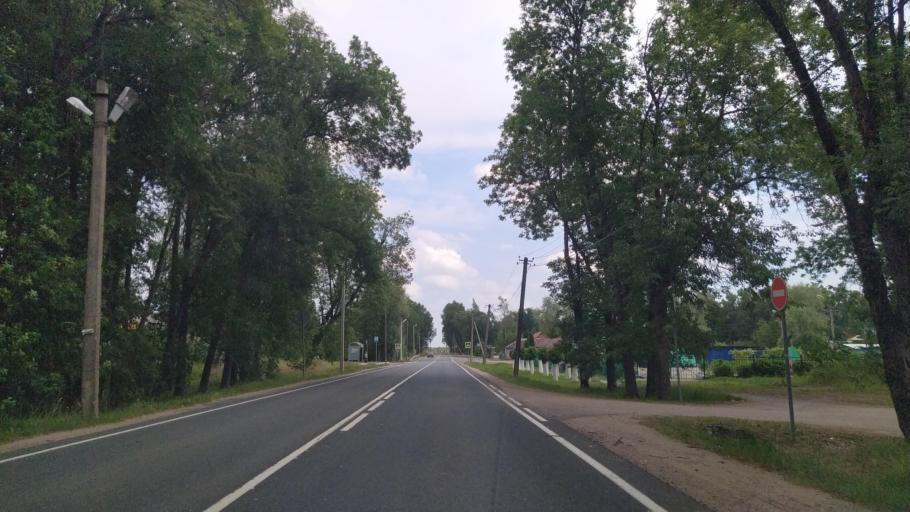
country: RU
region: Pskov
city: Pskov
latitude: 57.7615
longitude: 28.7600
